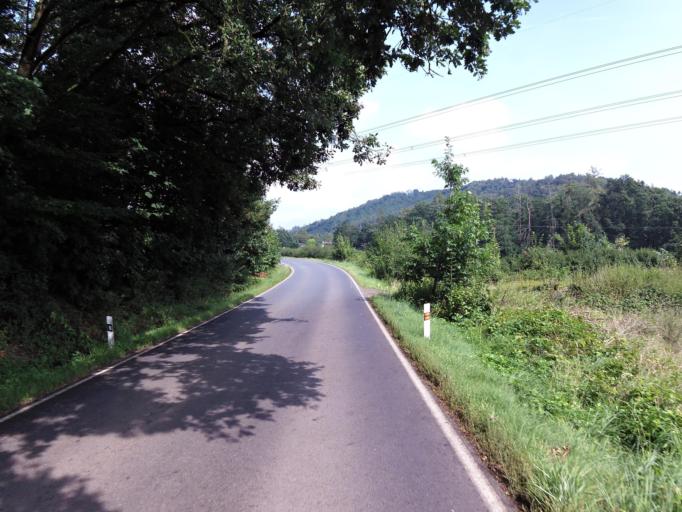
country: CZ
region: Central Bohemia
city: Tynec nad Sazavou
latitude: 49.8589
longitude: 14.5775
